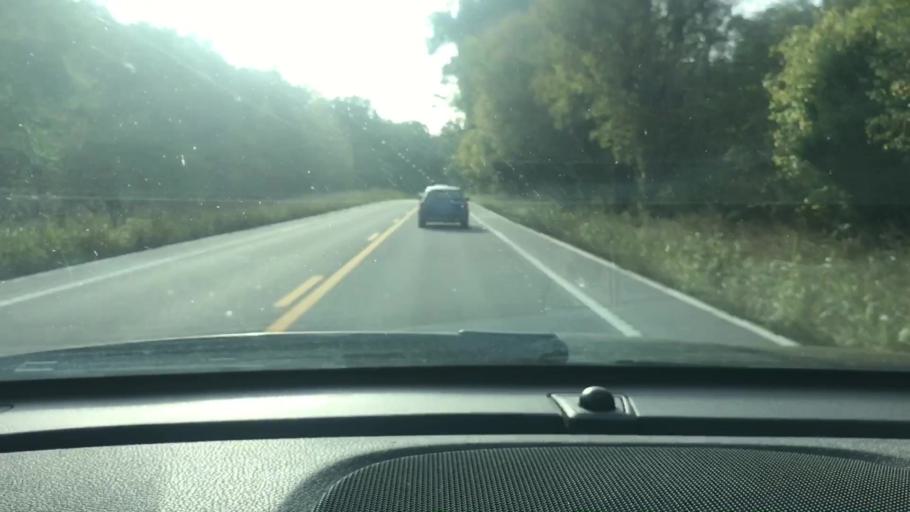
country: US
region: Tennessee
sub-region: Cheatham County
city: Pegram
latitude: 36.0144
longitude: -87.0403
